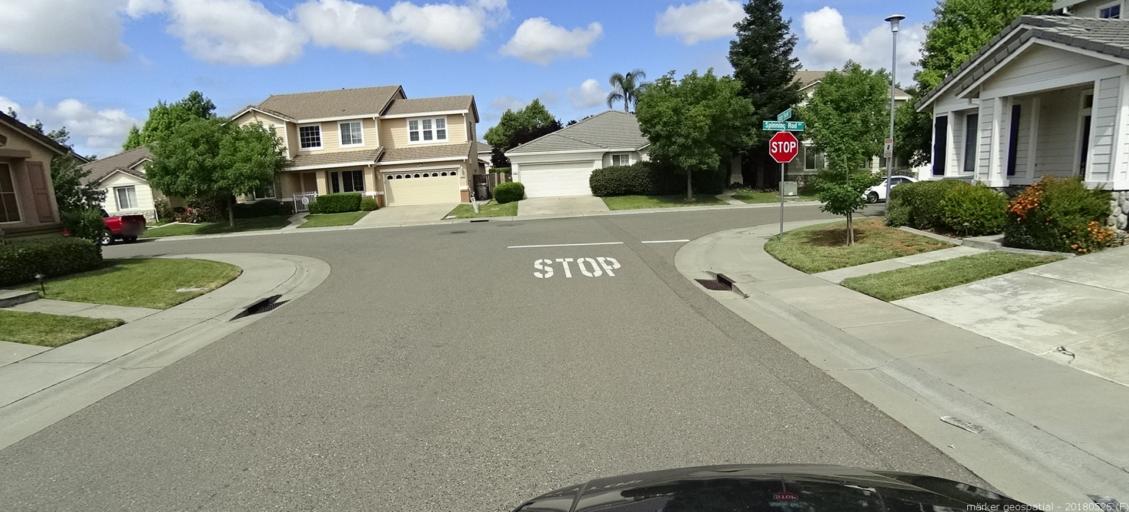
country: US
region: California
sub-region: Yolo County
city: West Sacramento
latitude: 38.6113
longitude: -121.5365
